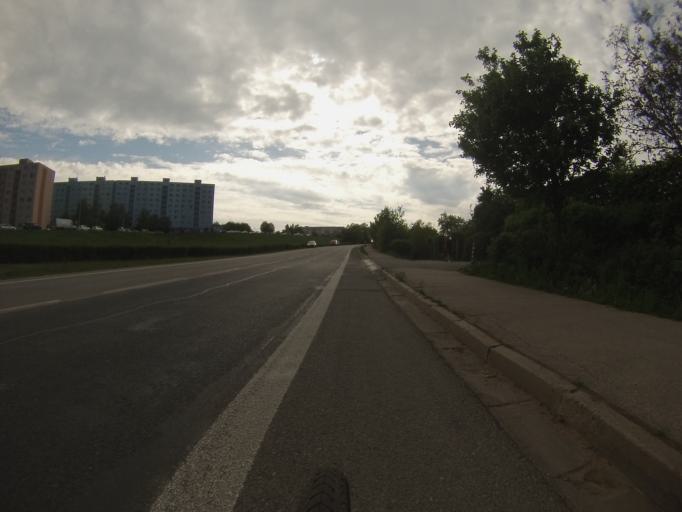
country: CZ
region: South Moravian
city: Troubsko
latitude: 49.2205
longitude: 16.5021
